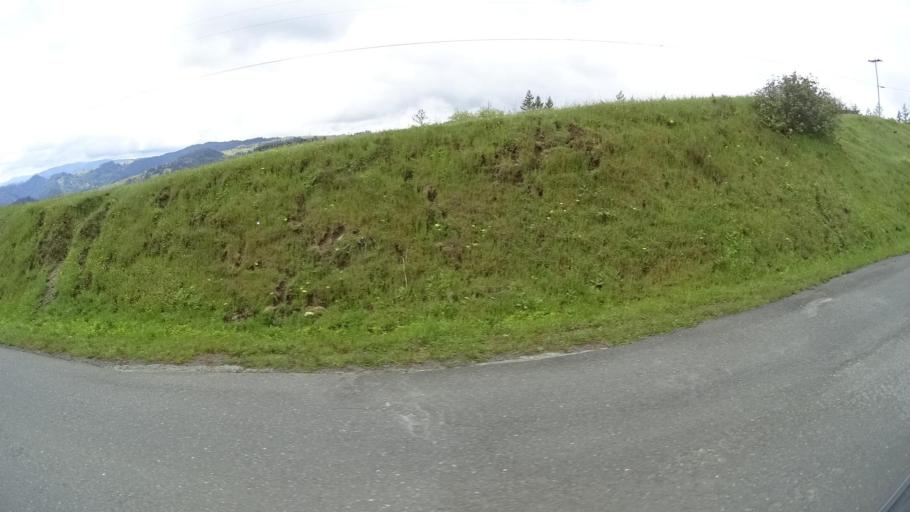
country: US
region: California
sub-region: Humboldt County
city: Redway
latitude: 40.1222
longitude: -123.6496
